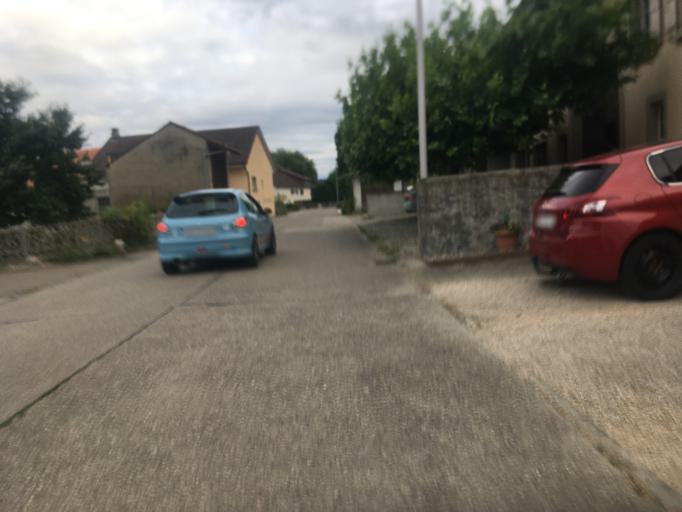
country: CH
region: Fribourg
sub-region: See District
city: Bas-Vully
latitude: 46.9649
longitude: 7.1118
